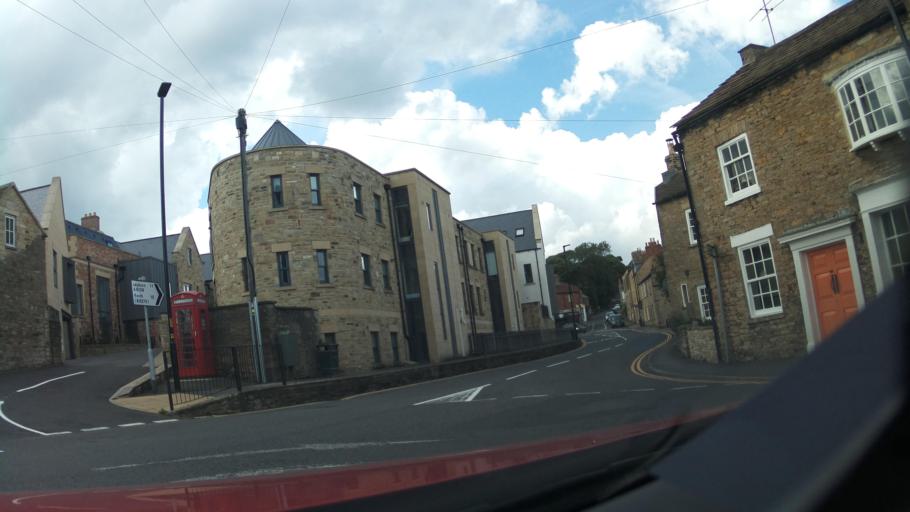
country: GB
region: England
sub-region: North Yorkshire
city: Catterick Garrison
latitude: 54.4046
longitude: -1.7434
